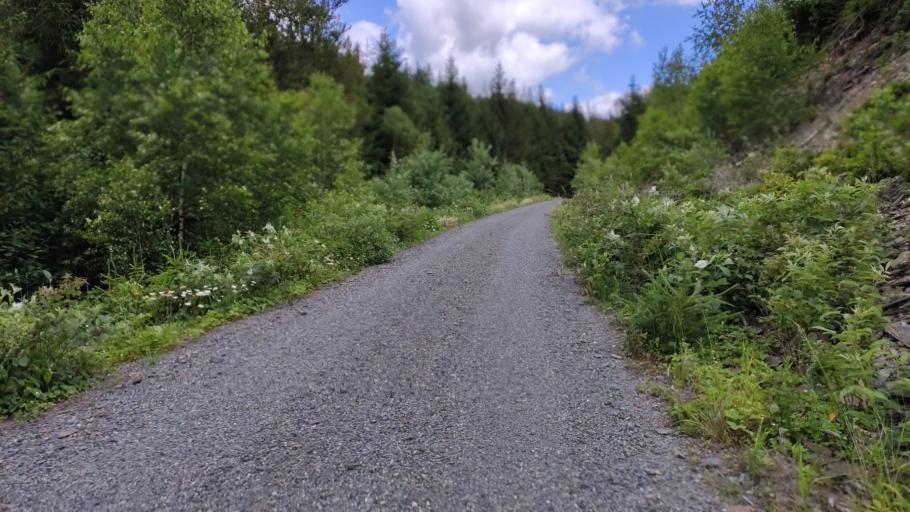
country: DE
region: Bavaria
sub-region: Upper Franconia
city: Tschirn
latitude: 50.3941
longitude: 11.4633
